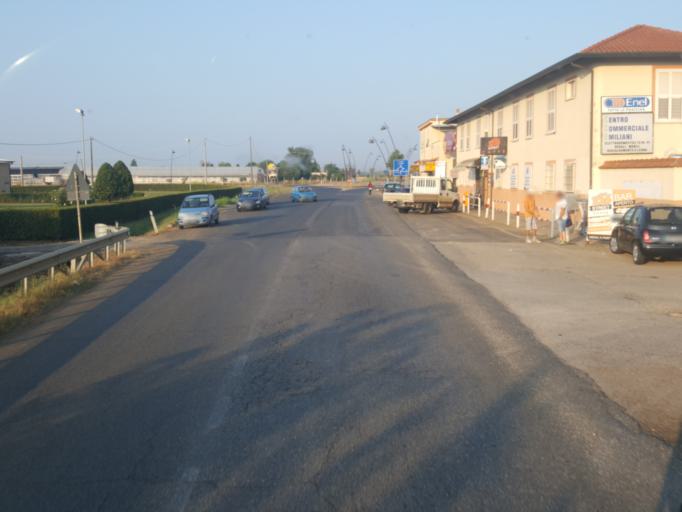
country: IT
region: Latium
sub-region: Provincia di Latina
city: Sezze Scalo
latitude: 41.4779
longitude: 13.0236
